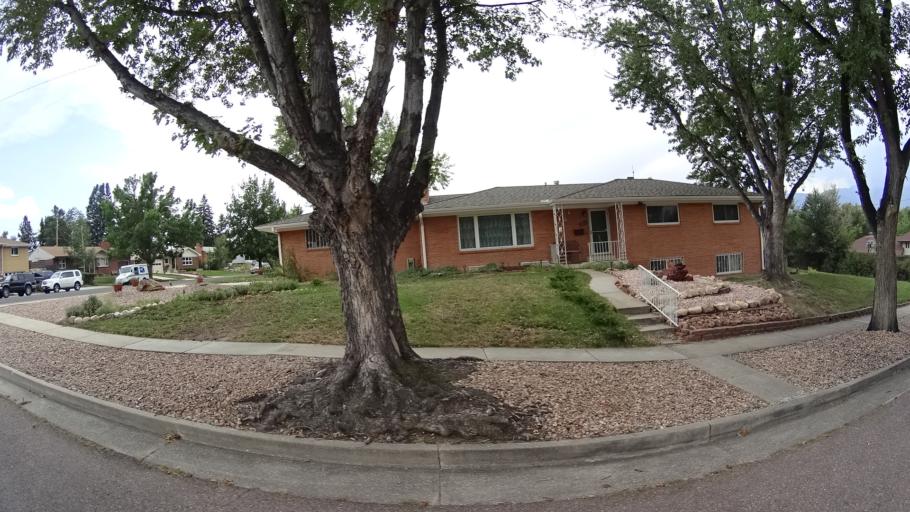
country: US
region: Colorado
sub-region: El Paso County
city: Colorado Springs
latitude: 38.8664
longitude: -104.7814
